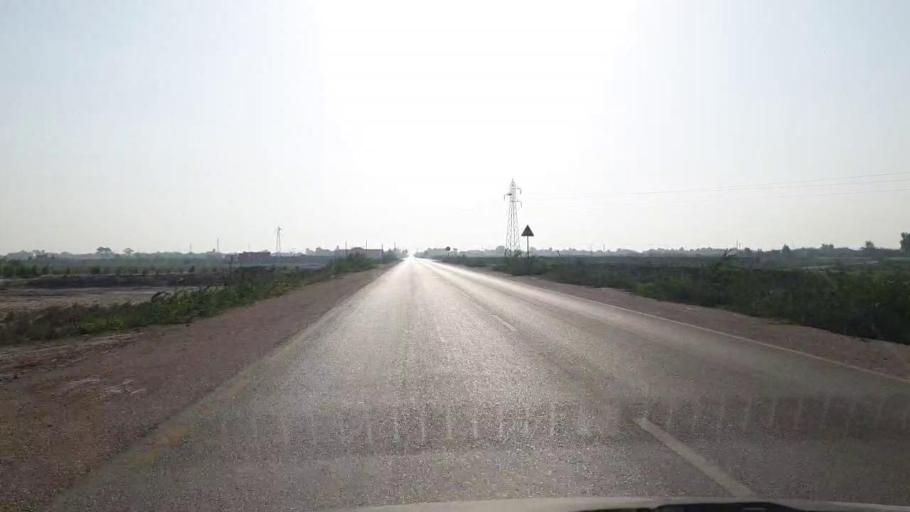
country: PK
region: Sindh
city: Badin
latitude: 24.6797
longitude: 68.8423
